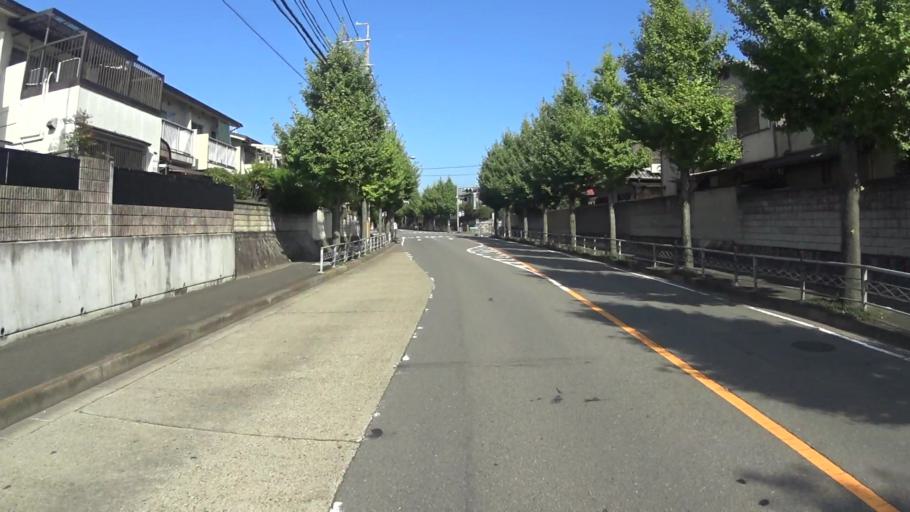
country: JP
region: Kyoto
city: Muko
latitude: 34.9591
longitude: 135.6855
